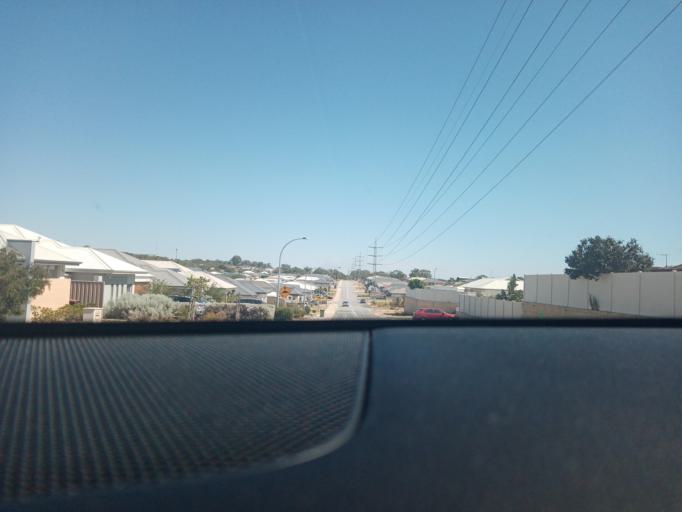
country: AU
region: Western Australia
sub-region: City of Cockburn
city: Beeliar
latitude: -32.1315
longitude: 115.8083
